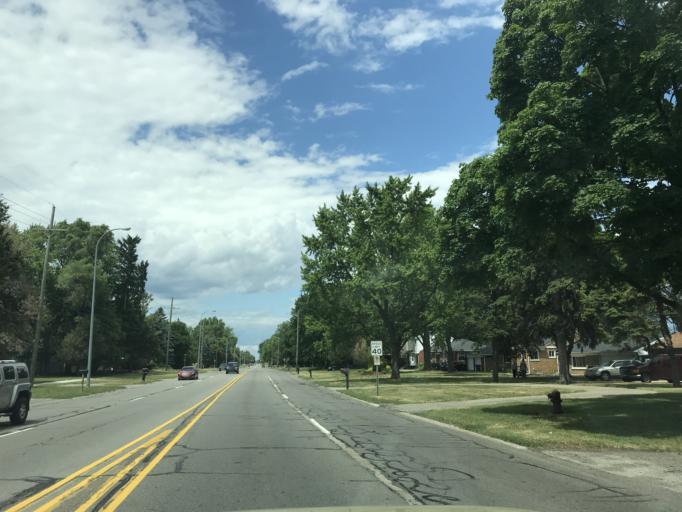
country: US
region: Michigan
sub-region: Wayne County
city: Redford
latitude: 42.3563
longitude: -83.3128
